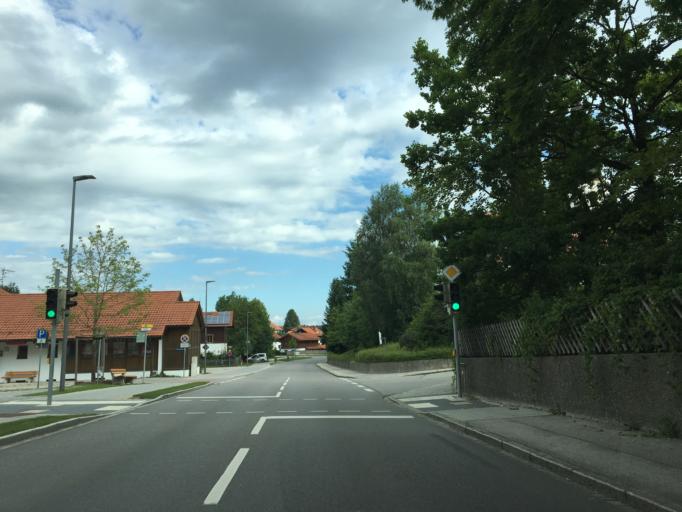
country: DE
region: Bavaria
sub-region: Upper Bavaria
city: Otterfing
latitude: 47.9106
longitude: 11.6748
